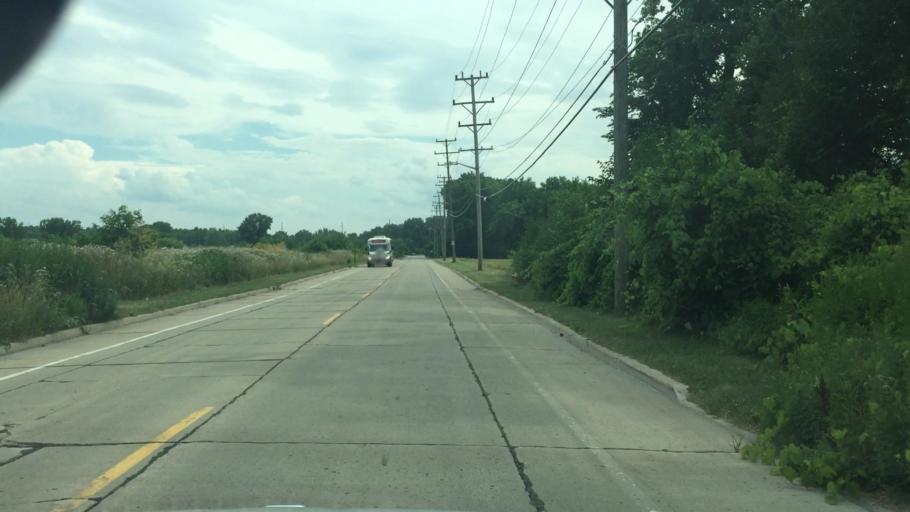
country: US
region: Michigan
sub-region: Monroe County
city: Monroe
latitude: 41.9137
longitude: -83.3731
